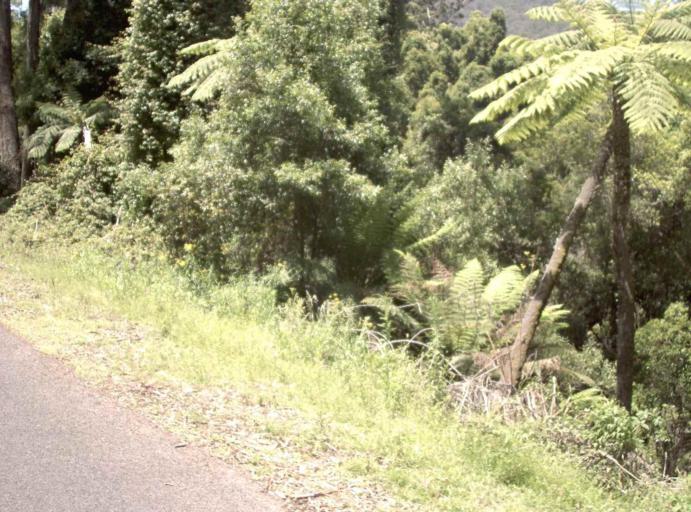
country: AU
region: New South Wales
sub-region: Bombala
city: Bombala
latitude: -37.4665
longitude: 148.9338
